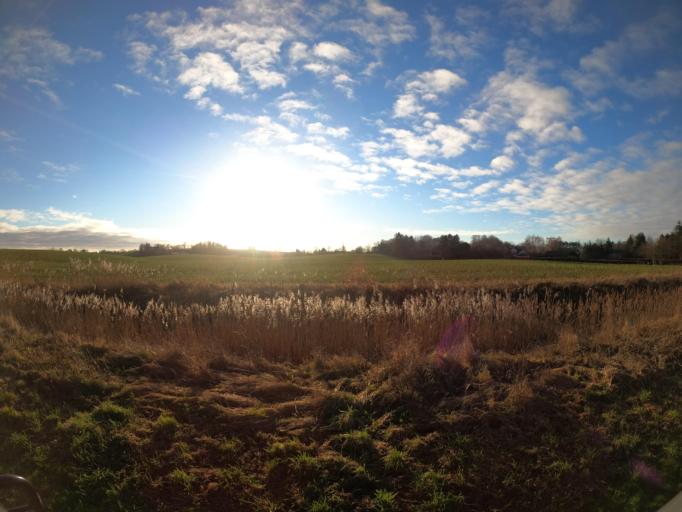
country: SE
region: Skane
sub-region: Svedala Kommun
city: Svedala
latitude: 55.5049
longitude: 13.2295
